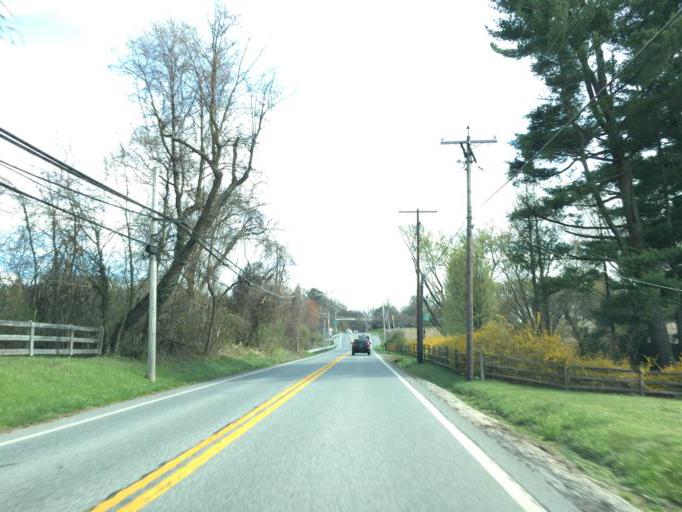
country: US
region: Maryland
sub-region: Baltimore County
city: Mays Chapel
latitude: 39.4501
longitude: -76.6864
